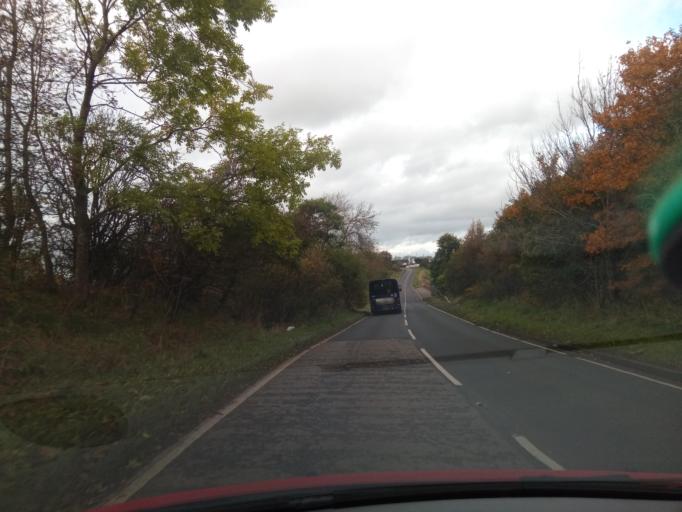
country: GB
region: Scotland
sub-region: West Lothian
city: Blackburn
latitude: 55.8475
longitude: -3.6123
